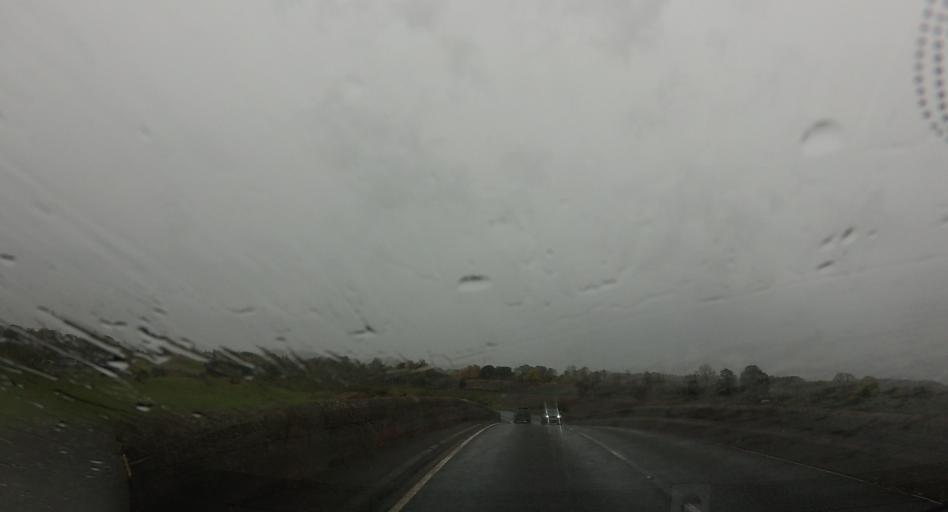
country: GB
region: Scotland
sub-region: Perth and Kinross
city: Coupar Angus
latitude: 56.5523
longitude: -3.2853
